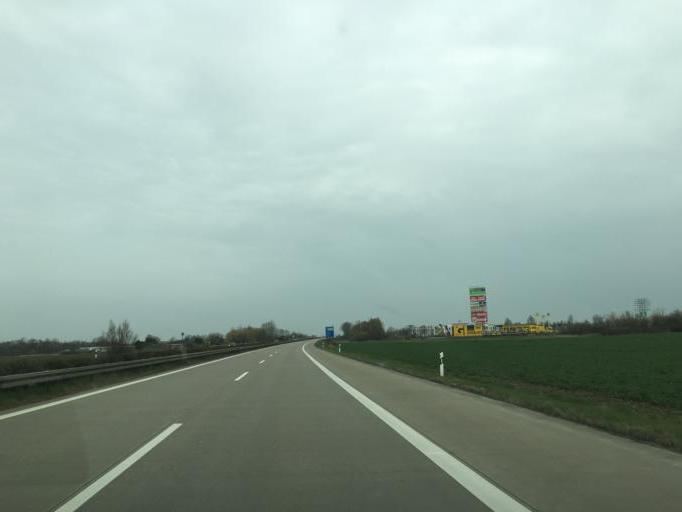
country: DE
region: Mecklenburg-Vorpommern
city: Roggentin
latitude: 54.0723
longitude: 12.1945
